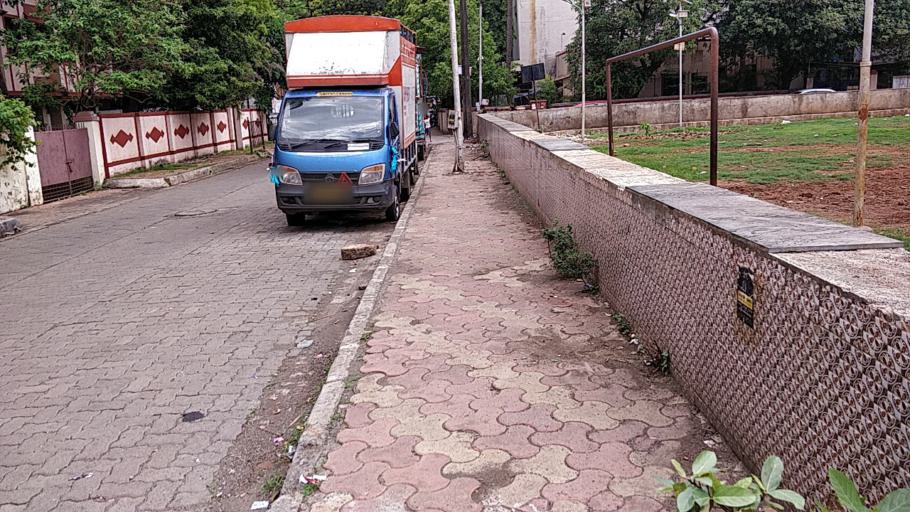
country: IN
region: Maharashtra
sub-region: Mumbai Suburban
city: Mumbai
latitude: 19.0773
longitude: 72.8611
